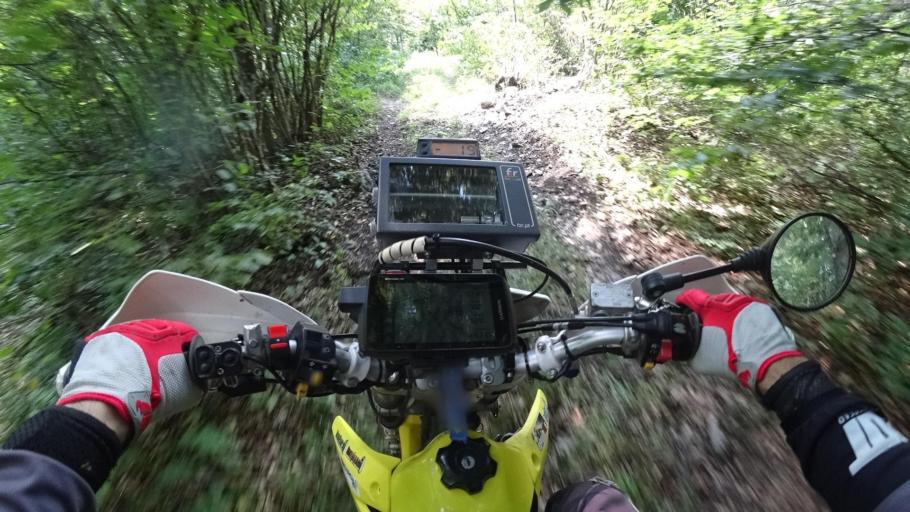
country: HR
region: Karlovacka
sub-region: Grad Ogulin
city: Ogulin
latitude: 45.2272
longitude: 15.1885
